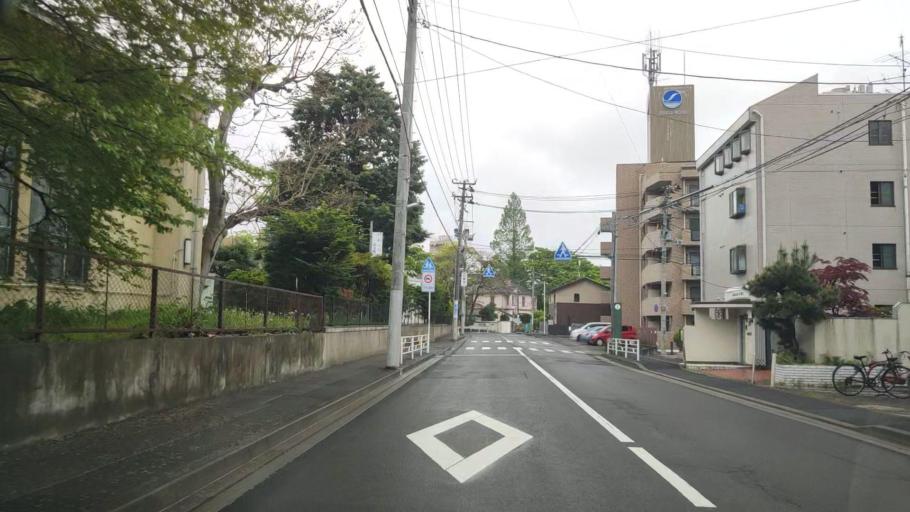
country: JP
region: Miyagi
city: Sendai
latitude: 38.2508
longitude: 140.8746
